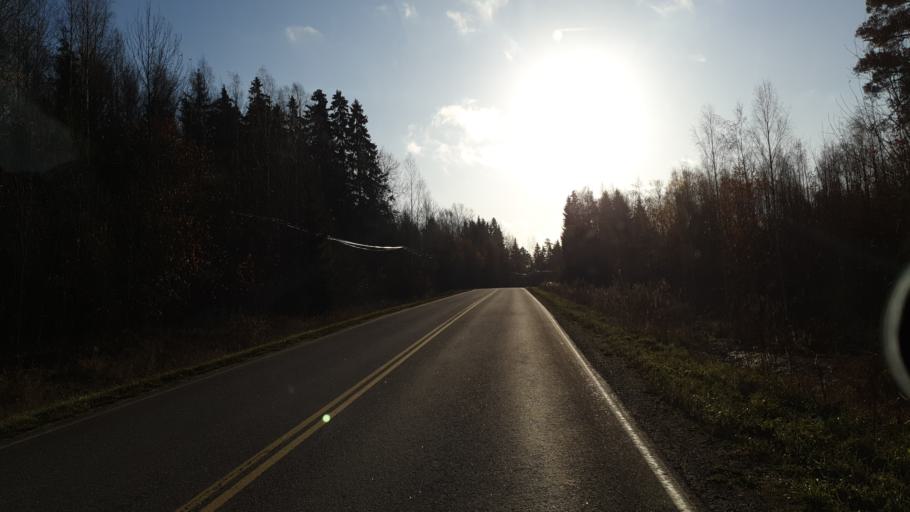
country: FI
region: Uusimaa
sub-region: Helsinki
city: Siuntio
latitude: 60.2051
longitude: 24.1855
